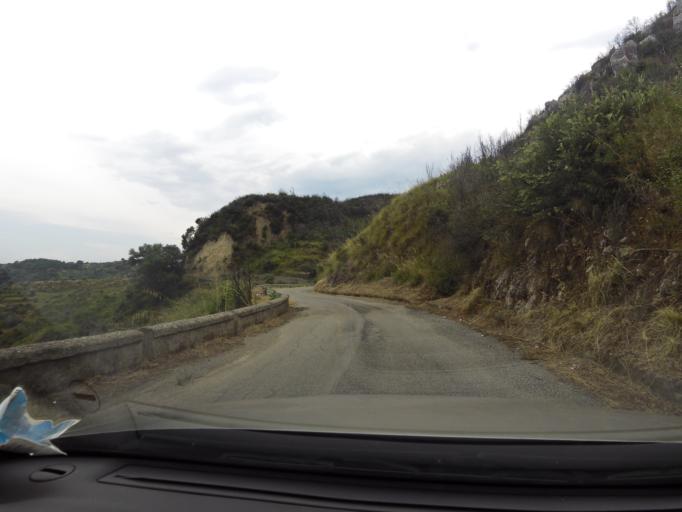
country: IT
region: Calabria
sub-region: Provincia di Reggio Calabria
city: Pazzano
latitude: 38.4623
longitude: 16.4494
